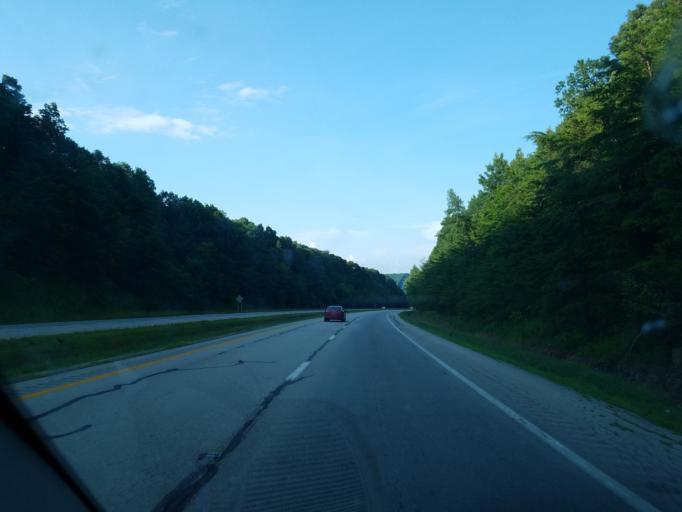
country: US
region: Ohio
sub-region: Adams County
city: Peebles
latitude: 39.0227
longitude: -83.2750
